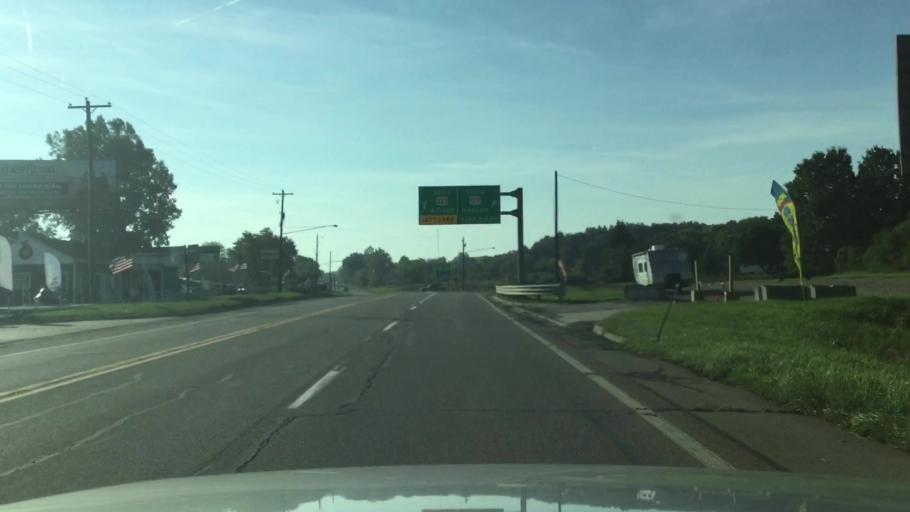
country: US
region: Michigan
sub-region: Lenawee County
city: Manitou Beach-Devils Lake
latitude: 42.0400
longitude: -84.3521
